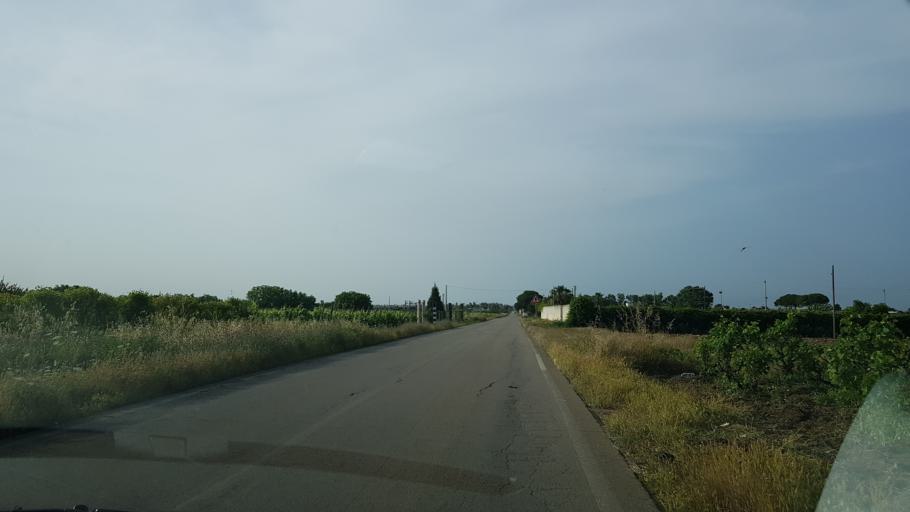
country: IT
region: Apulia
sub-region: Provincia di Brindisi
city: San Pancrazio Salentino
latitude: 40.3989
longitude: 17.8351
